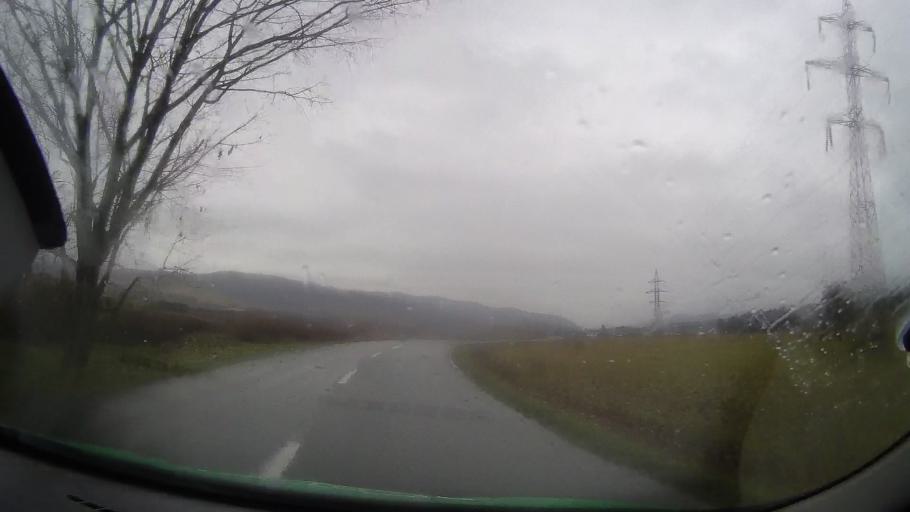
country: RO
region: Bistrita-Nasaud
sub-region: Comuna Mariselu
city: Mariselu
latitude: 47.0295
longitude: 24.4920
